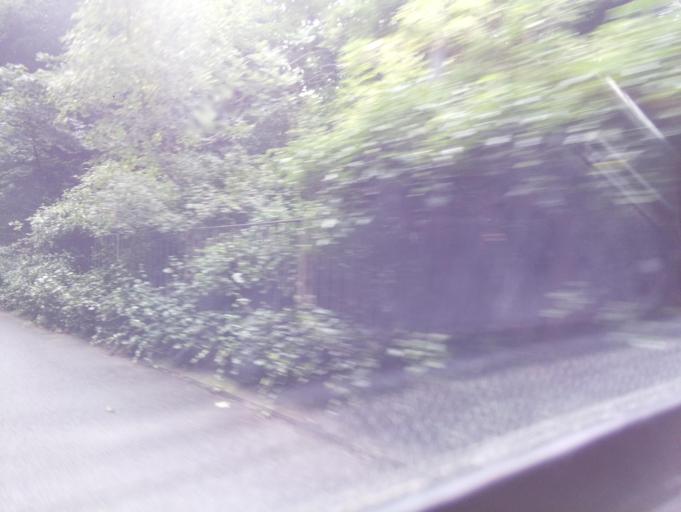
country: GB
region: England
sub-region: Kirklees
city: Holmfirth
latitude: 53.5744
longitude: -1.7532
